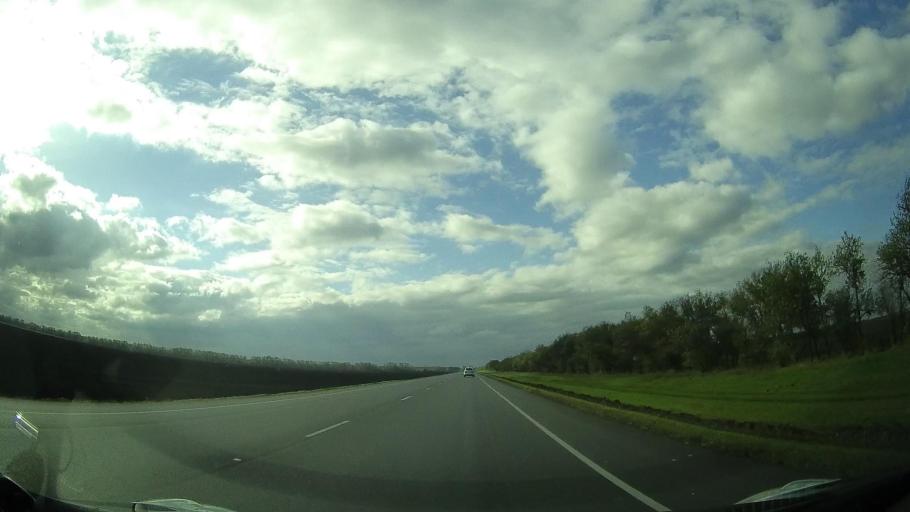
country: RU
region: Rostov
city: Tselina
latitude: 46.5320
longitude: 40.9361
